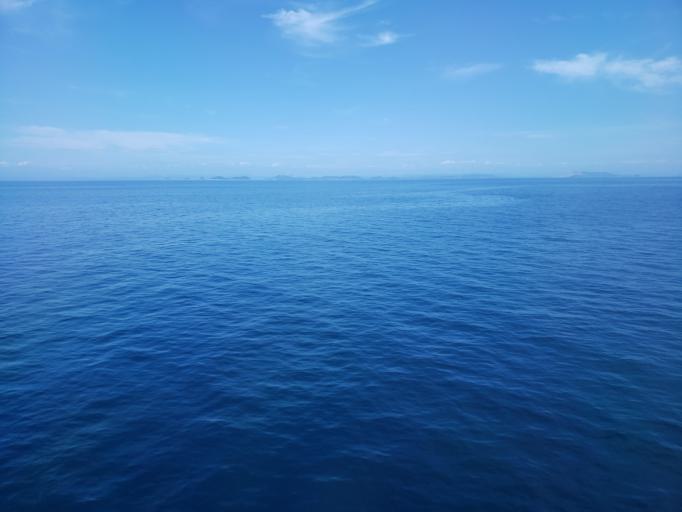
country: JP
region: Hyogo
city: Fukura
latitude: 34.4907
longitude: 134.5597
